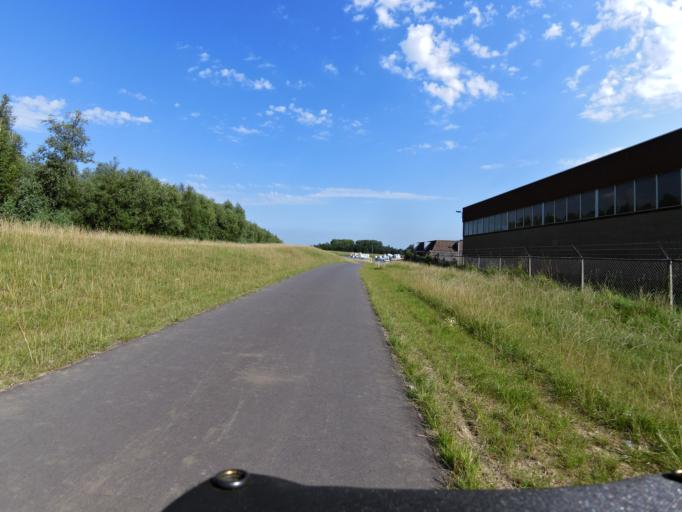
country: NL
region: South Holland
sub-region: Gemeente Binnenmaas
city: Heinenoord
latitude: 51.8290
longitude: 4.4603
